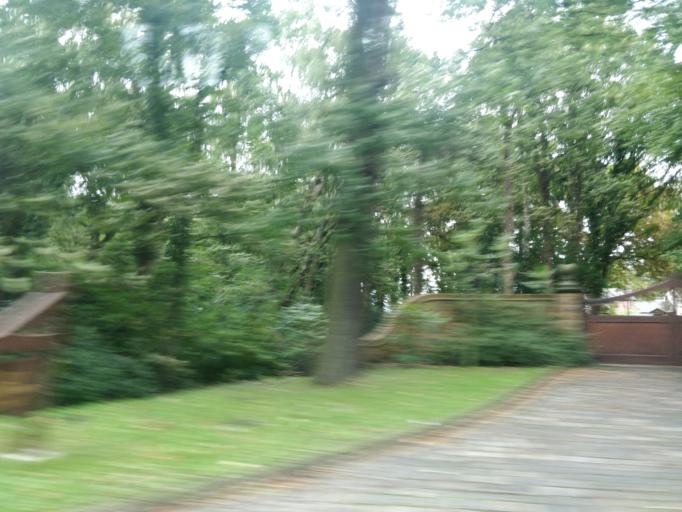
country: GB
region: England
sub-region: Lancashire
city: Ormskirk
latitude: 53.6048
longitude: -2.9115
